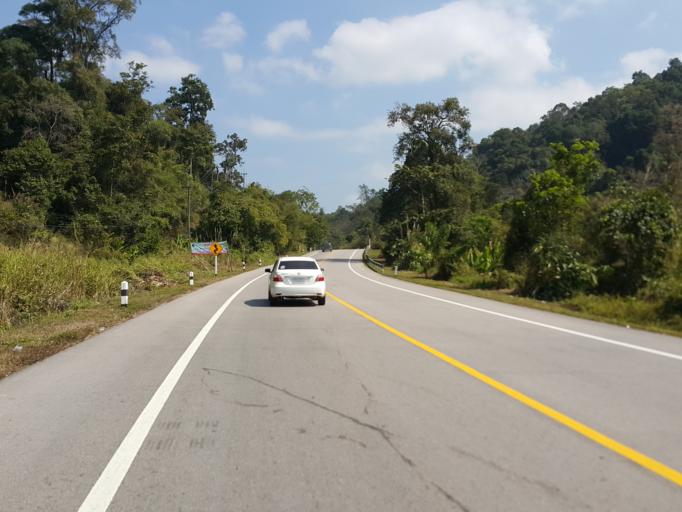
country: TH
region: Chiang Mai
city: Mae On
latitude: 19.0476
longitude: 99.3456
